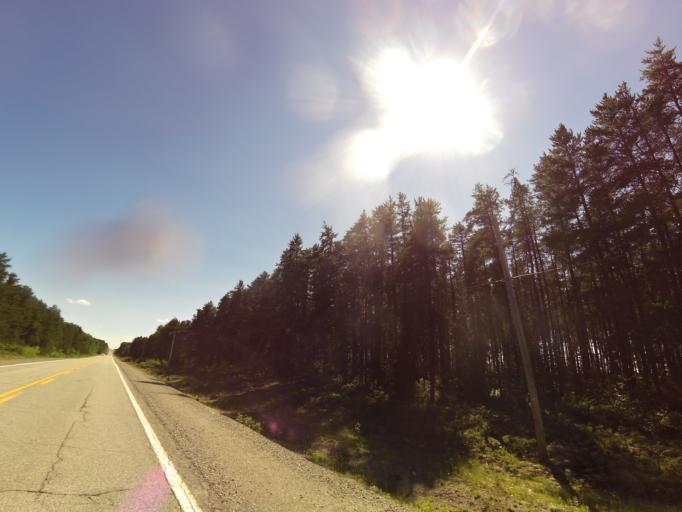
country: CA
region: Quebec
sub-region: Abitibi-Temiscamingue
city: Senneterre
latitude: 48.1238
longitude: -77.3842
